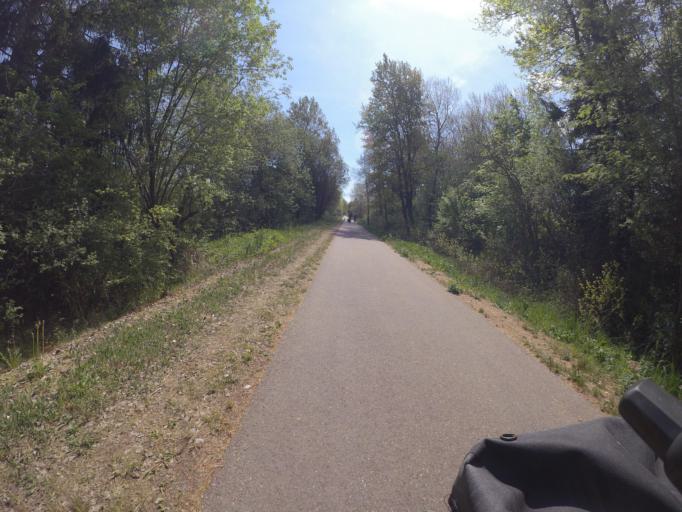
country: BE
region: Wallonia
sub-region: Province de Liege
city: Bullange
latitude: 50.4228
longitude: 6.2460
